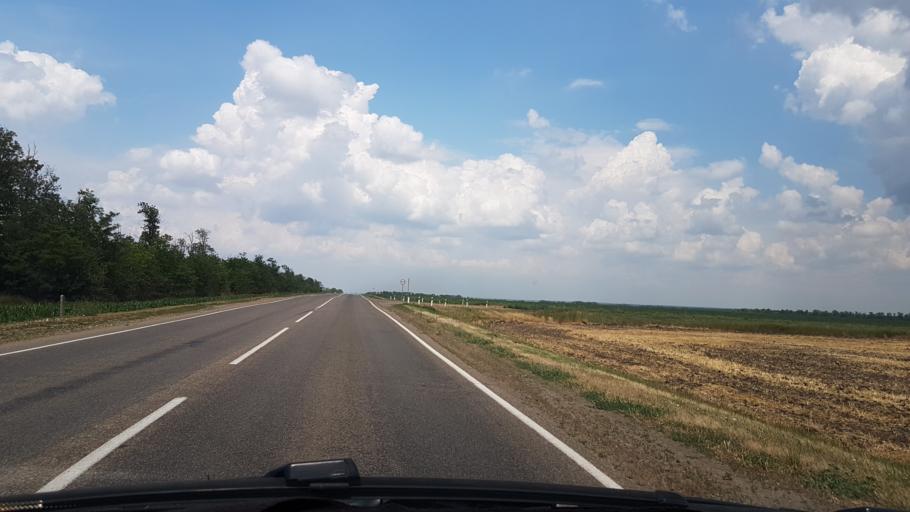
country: RU
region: Krasnodarskiy
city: Dmitriyevskaya
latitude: 45.6792
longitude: 40.7440
